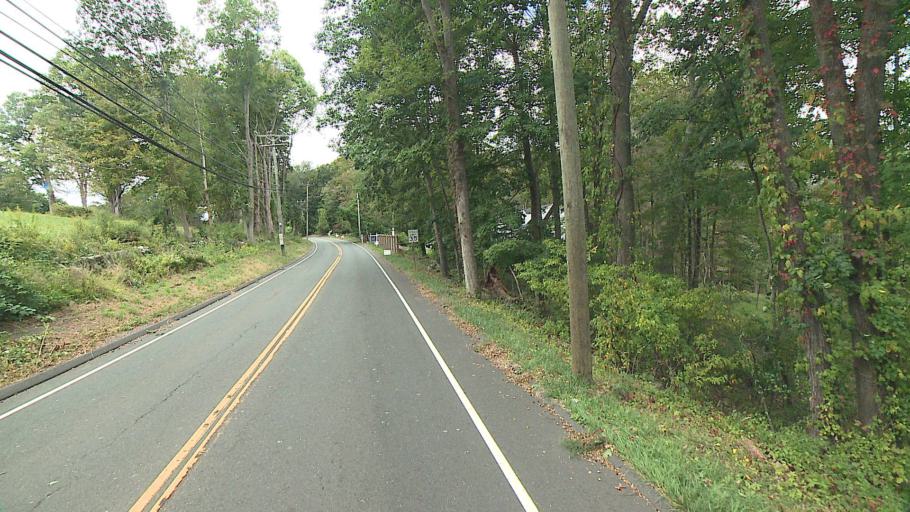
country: US
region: Connecticut
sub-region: Fairfield County
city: Wilton
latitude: 41.1993
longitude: -73.4431
